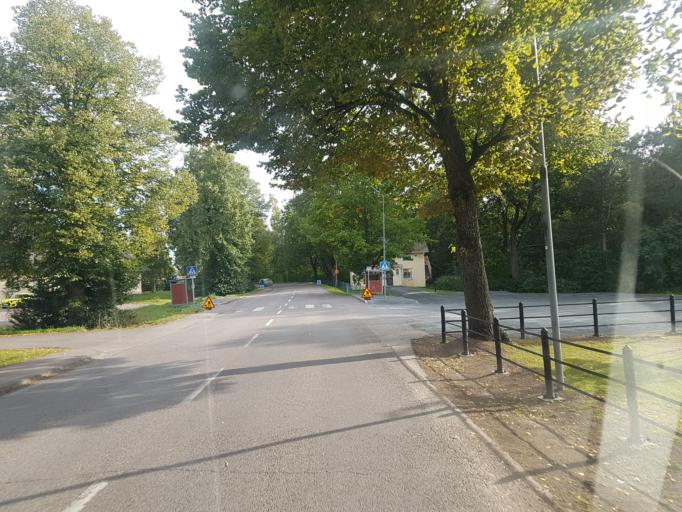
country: SE
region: Dalarna
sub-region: Borlange Kommun
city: Ornas
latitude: 60.4130
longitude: 15.6093
